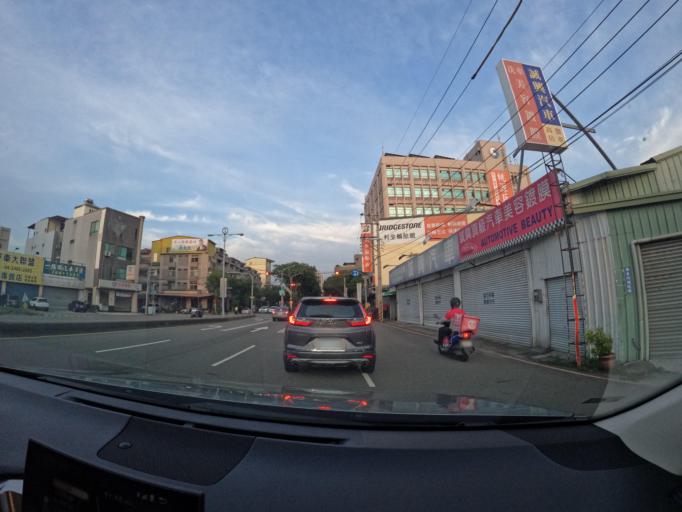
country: TW
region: Taiwan
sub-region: Taichung City
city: Taichung
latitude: 24.1190
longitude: 120.6845
